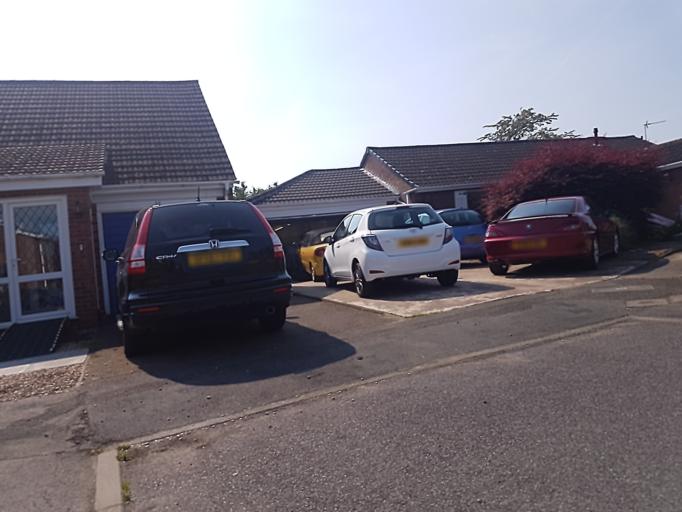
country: GB
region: England
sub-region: Leicestershire
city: Hinckley
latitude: 52.5508
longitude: -1.3591
